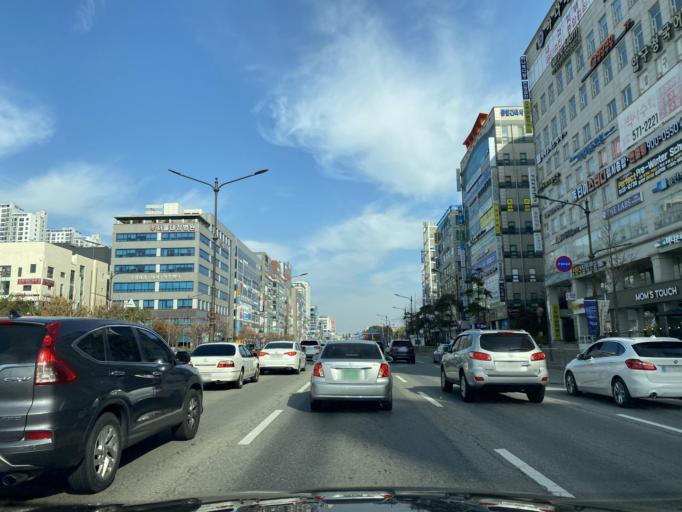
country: KR
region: Chungcheongnam-do
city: Cheonan
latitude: 36.8103
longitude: 127.1081
